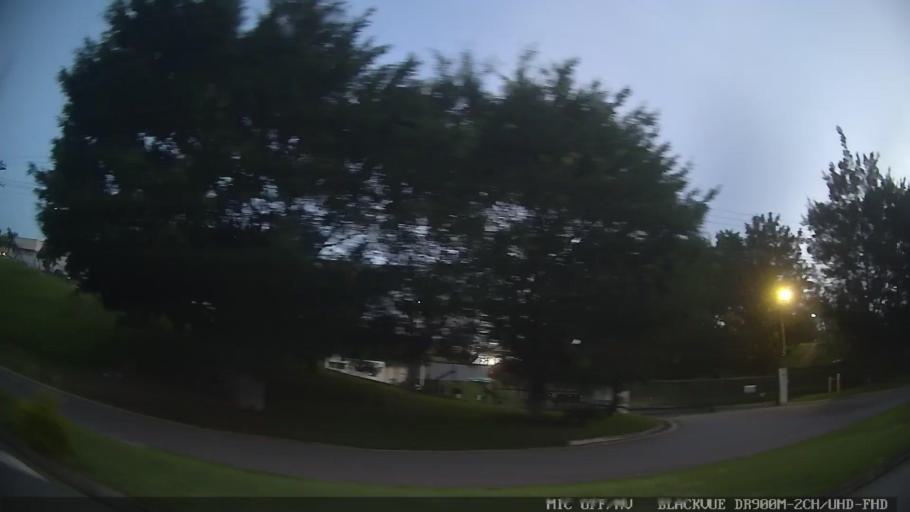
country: BR
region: Sao Paulo
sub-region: Cabreuva
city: Cabreuva
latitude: -23.2490
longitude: -47.0773
